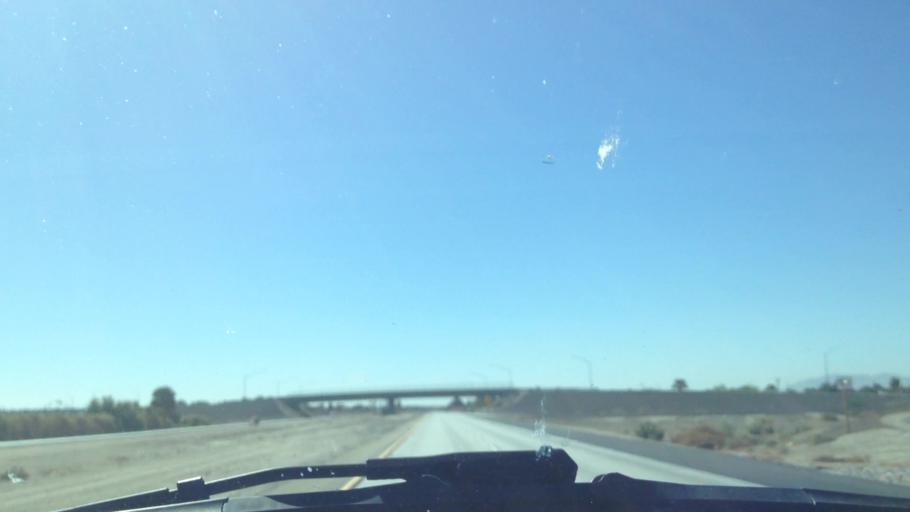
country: US
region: California
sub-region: Riverside County
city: Thermal
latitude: 33.6447
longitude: -116.1351
